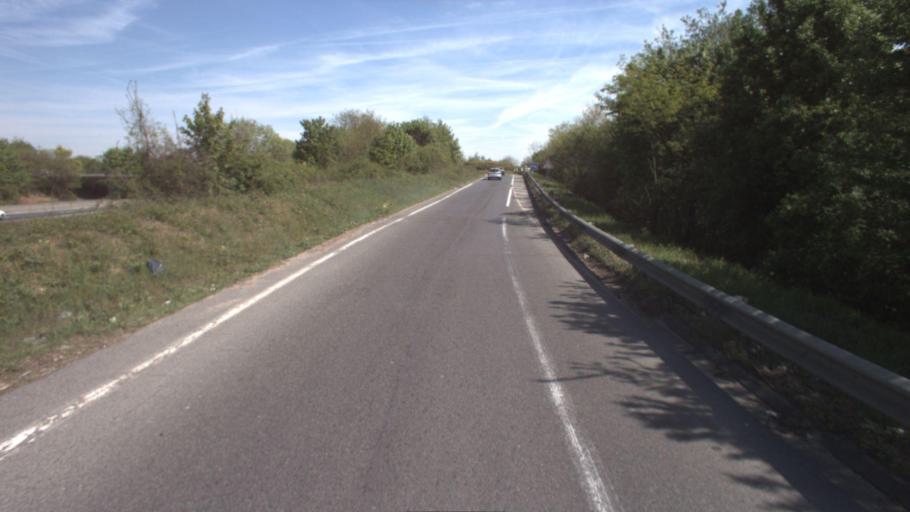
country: FR
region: Ile-de-France
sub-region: Departement de Seine-et-Marne
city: Saint-Mard
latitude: 49.0567
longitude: 2.7013
